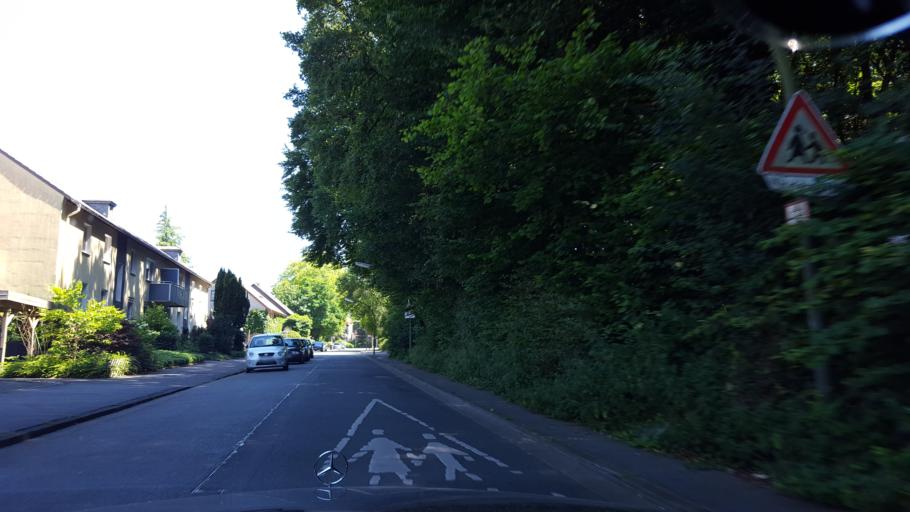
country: DE
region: North Rhine-Westphalia
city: Marl
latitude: 51.6619
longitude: 7.1341
